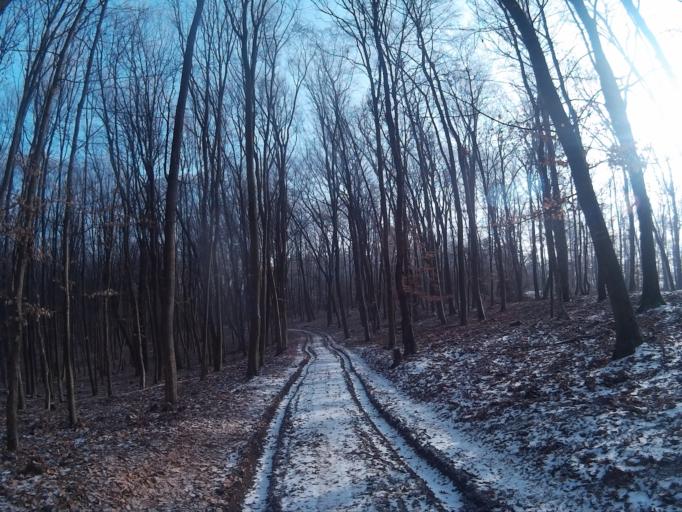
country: HU
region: Borsod-Abauj-Zemplen
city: Szendro
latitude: 48.4953
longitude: 20.7693
